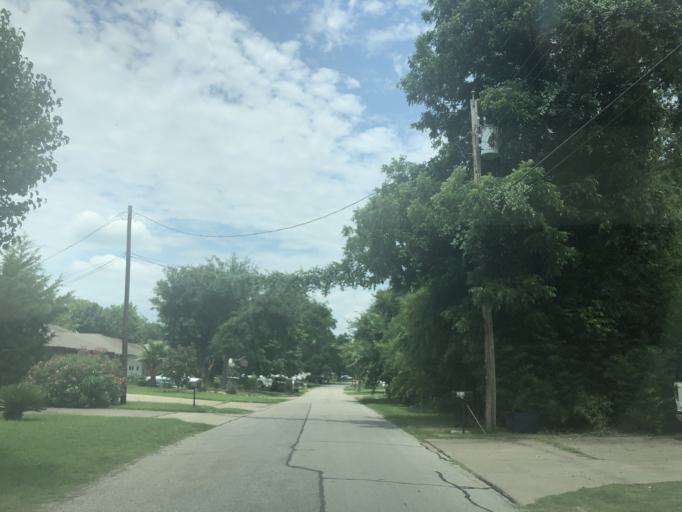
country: US
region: Texas
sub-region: Dallas County
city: Irving
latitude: 32.7880
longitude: -96.9352
